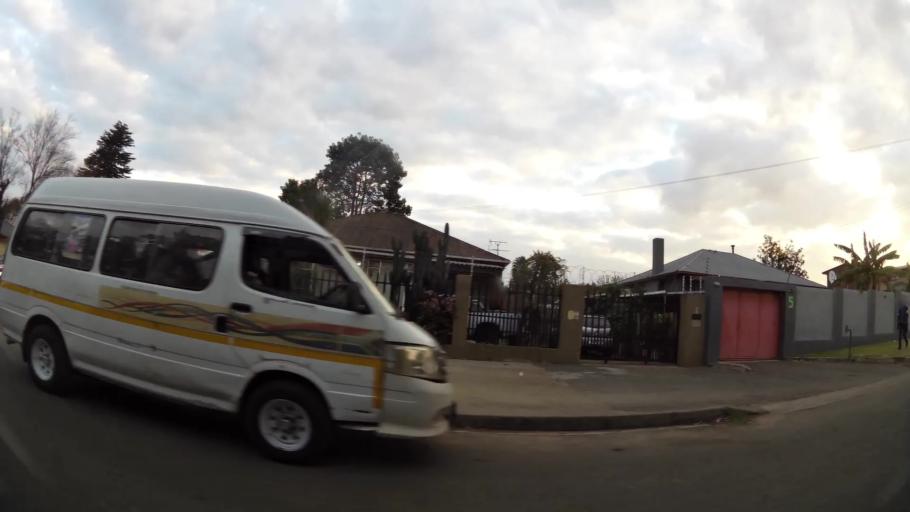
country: ZA
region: Gauteng
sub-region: Ekurhuleni Metropolitan Municipality
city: Germiston
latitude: -26.1945
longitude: 28.1532
